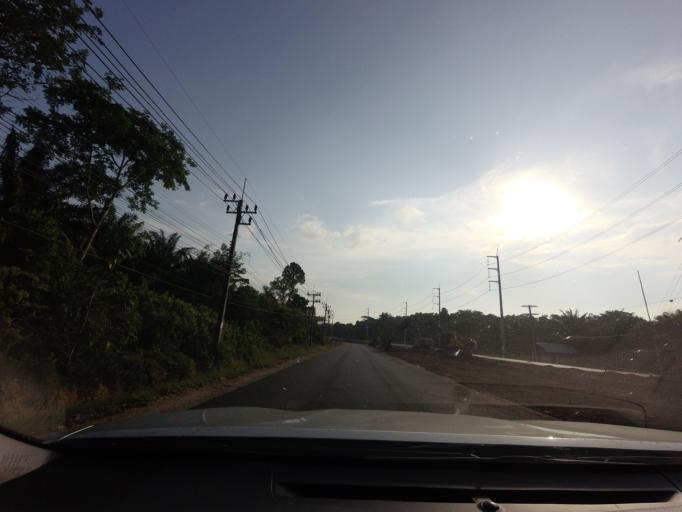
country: TH
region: Phangnga
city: Ban Khao Lak
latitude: 8.7372
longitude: 98.2556
